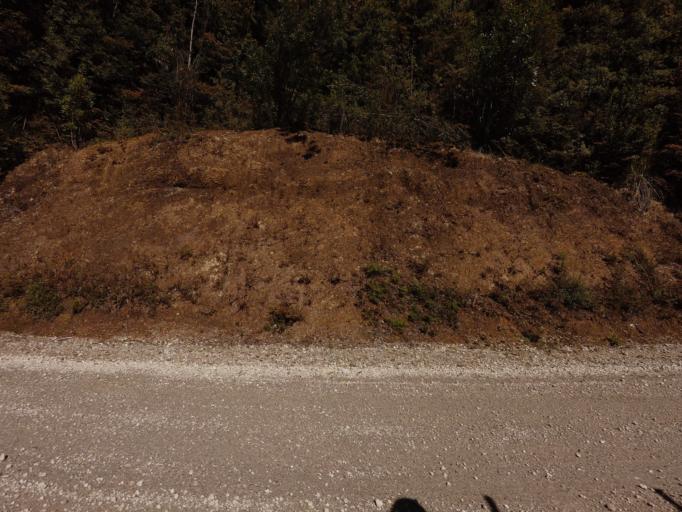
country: AU
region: Tasmania
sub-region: Huon Valley
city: Geeveston
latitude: -42.8421
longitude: 146.3759
